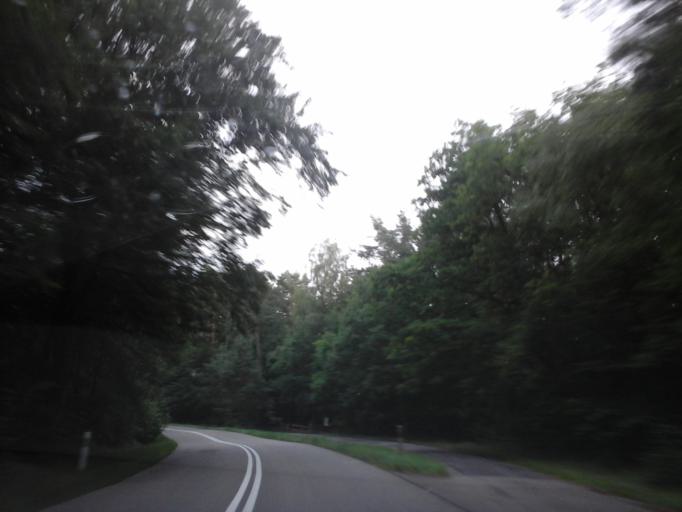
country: PL
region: West Pomeranian Voivodeship
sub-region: Powiat kamienski
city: Golczewo
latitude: 53.7852
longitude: 15.0177
